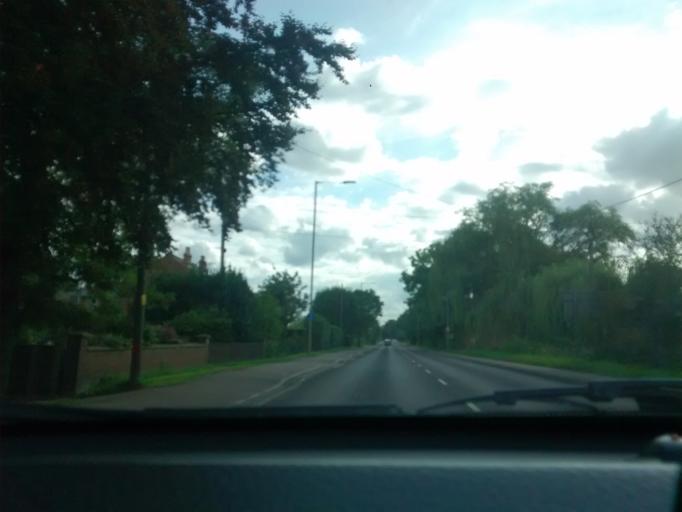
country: GB
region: England
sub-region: Norfolk
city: King's Lynn
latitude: 52.7300
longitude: 0.4158
